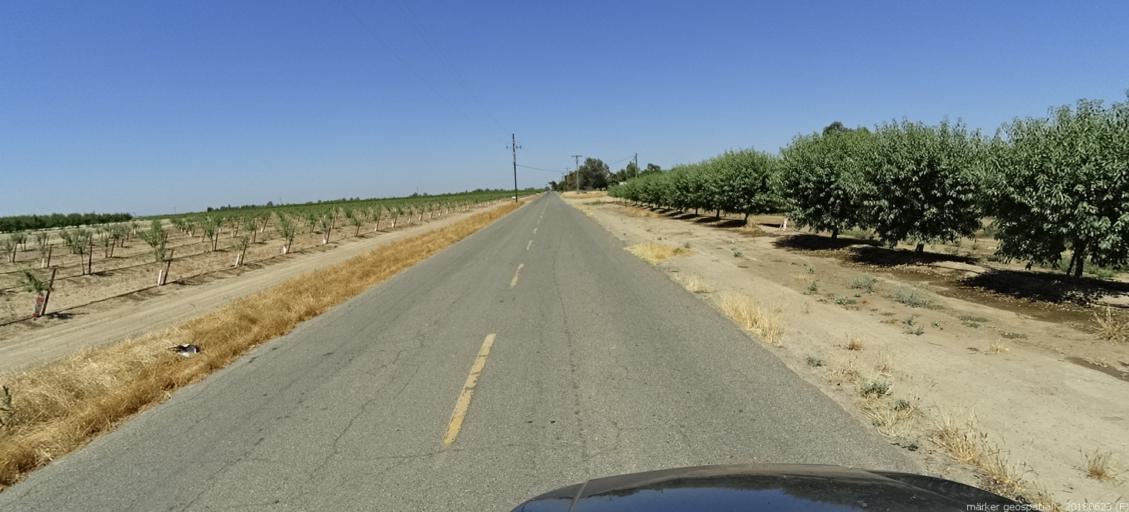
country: US
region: California
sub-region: Madera County
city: Chowchilla
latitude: 37.0983
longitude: -120.2336
